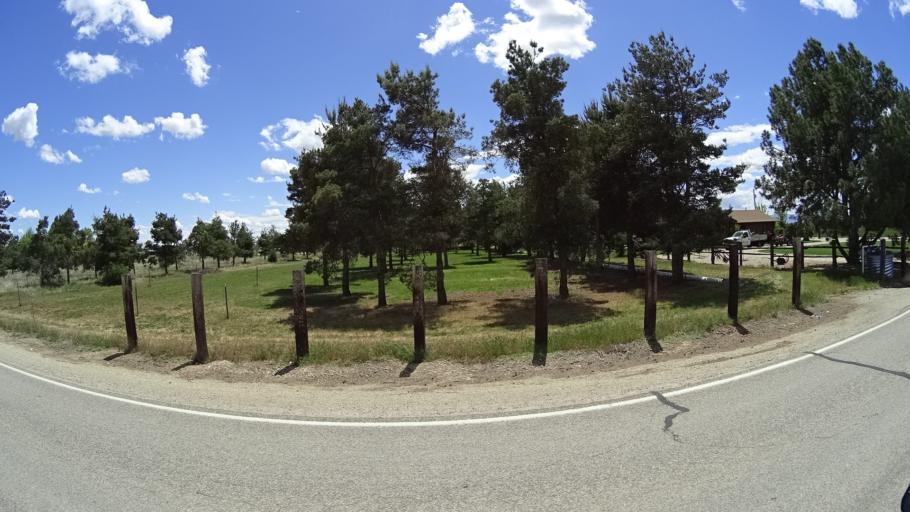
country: US
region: Idaho
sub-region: Ada County
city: Meridian
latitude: 43.5830
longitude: -116.4477
